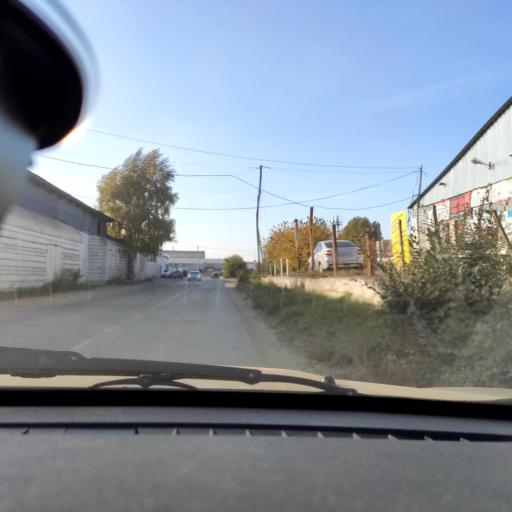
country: RU
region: Samara
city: Zhigulevsk
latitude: 53.5217
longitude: 49.4721
